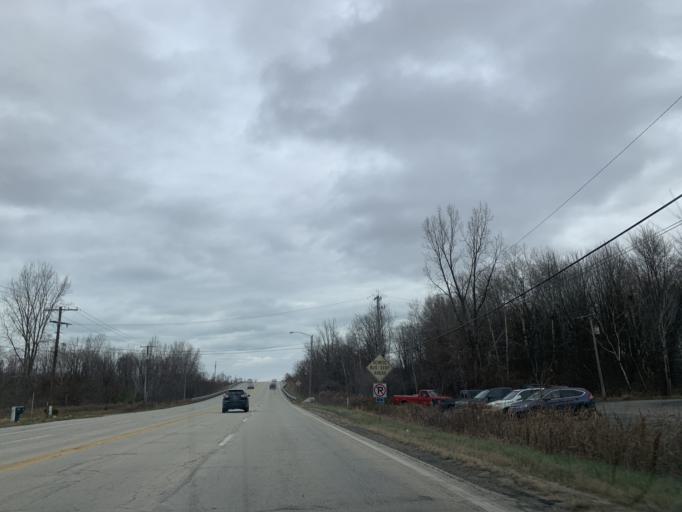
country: US
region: Indiana
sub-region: LaPorte County
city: Trail Creek
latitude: 41.7121
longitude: -86.8259
